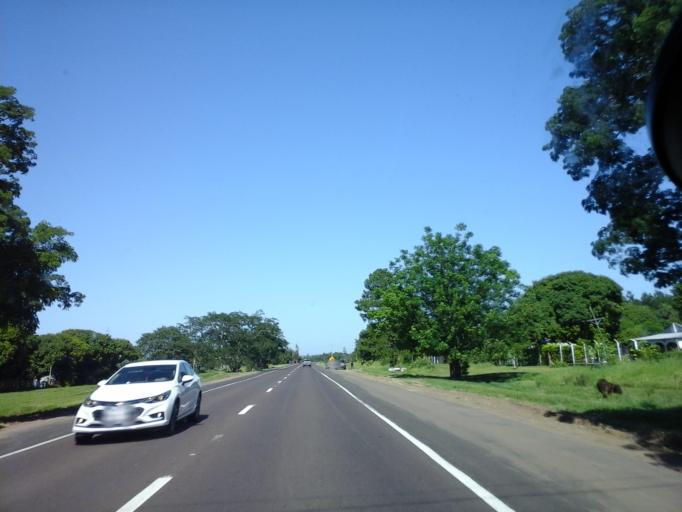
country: AR
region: Corrientes
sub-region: Departamento de San Cosme
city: San Cosme
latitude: -27.3683
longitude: -58.4177
